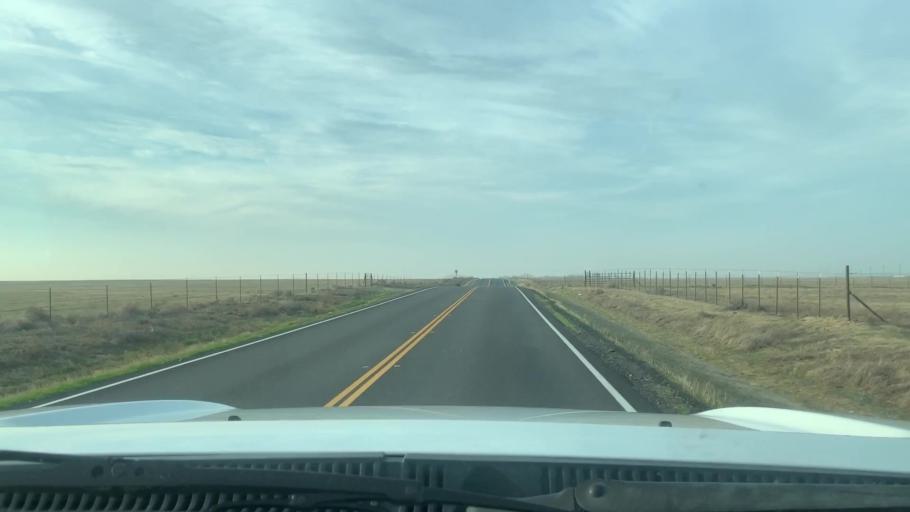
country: US
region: California
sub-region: Kern County
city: Lost Hills
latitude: 35.5932
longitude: -119.8410
